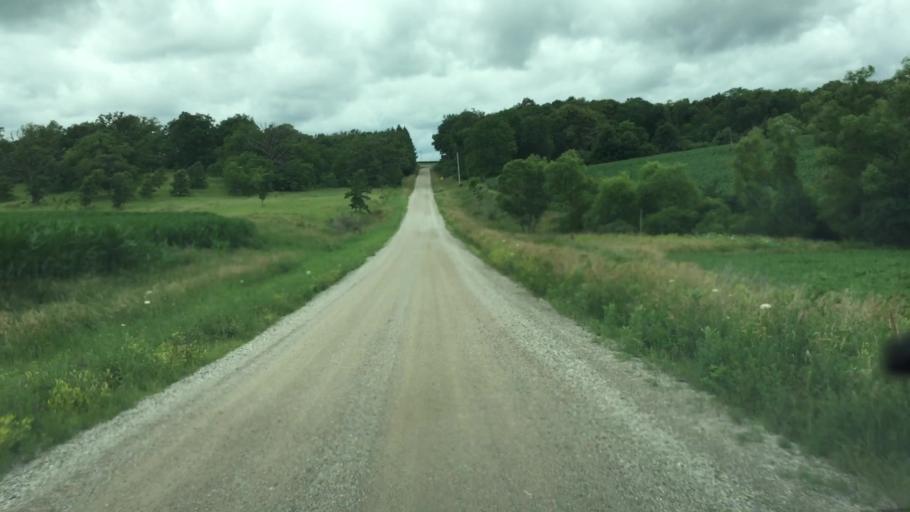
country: US
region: Iowa
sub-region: Jasper County
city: Monroe
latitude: 41.5952
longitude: -93.1097
